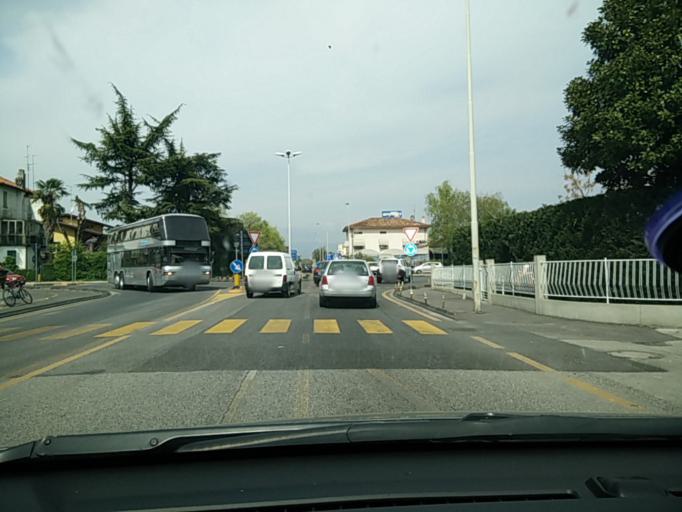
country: IT
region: Friuli Venezia Giulia
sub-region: Provincia di Pordenone
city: Pordenone
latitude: 45.9612
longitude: 12.6769
